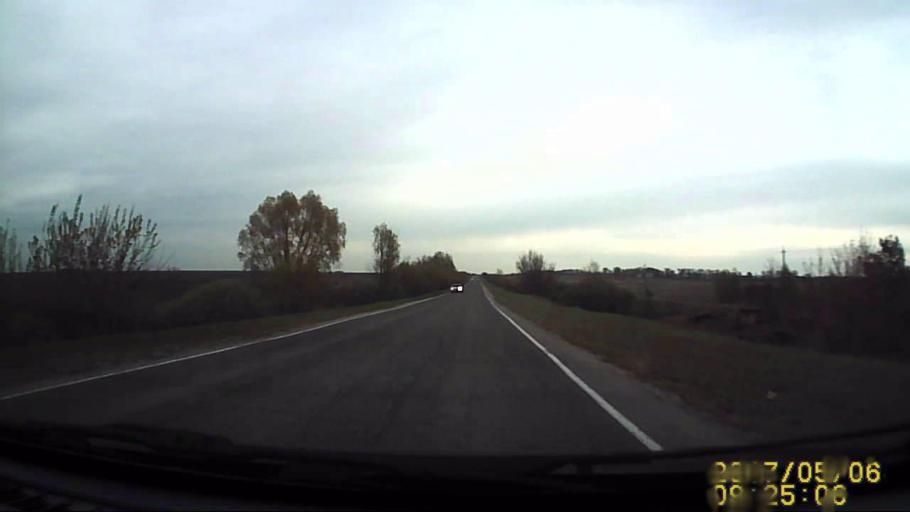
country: RU
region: Ulyanovsk
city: Cherdakly
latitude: 54.3816
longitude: 48.8165
